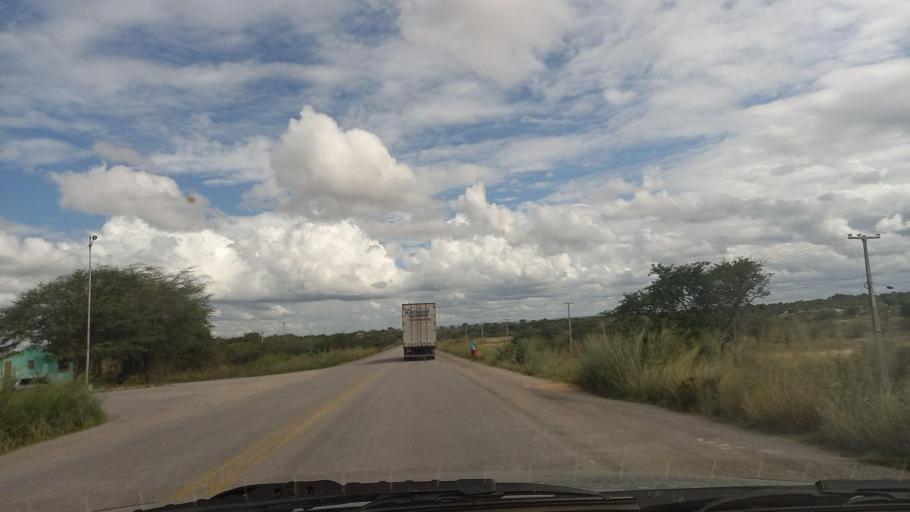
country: BR
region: Pernambuco
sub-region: Cachoeirinha
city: Cachoeirinha
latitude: -8.4070
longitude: -36.1870
